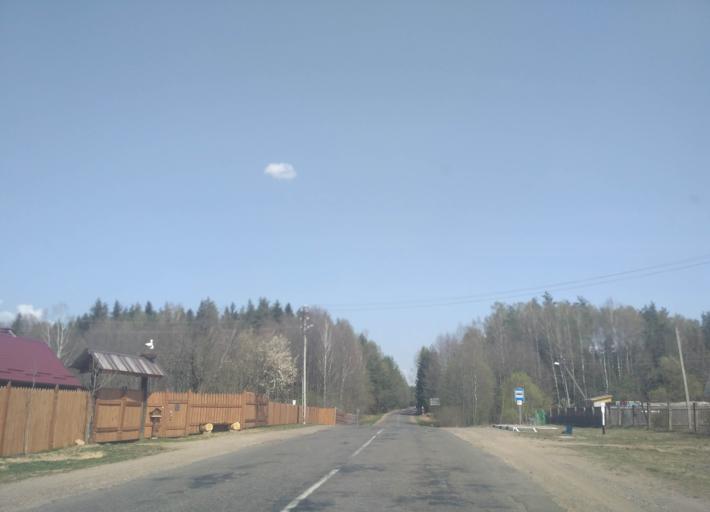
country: BY
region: Minsk
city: Loshnitsa
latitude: 54.4217
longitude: 28.6473
